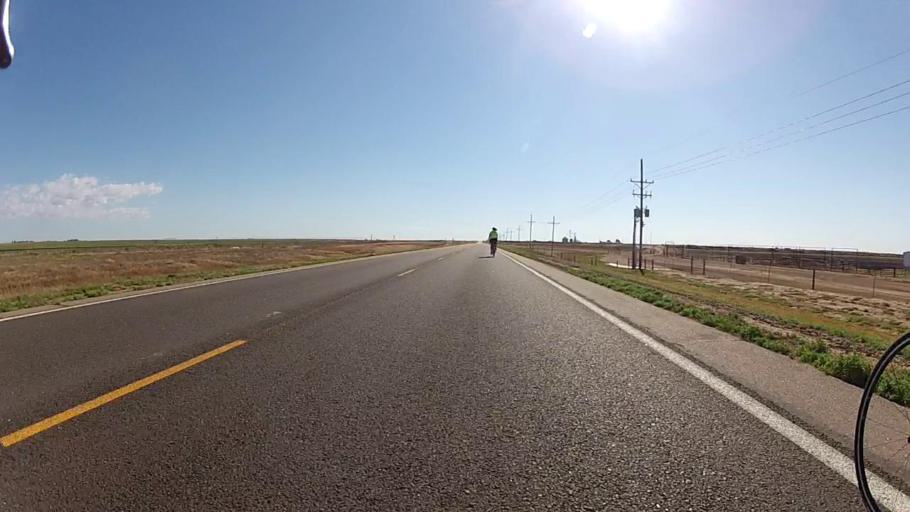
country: US
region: Kansas
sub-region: Gray County
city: Cimarron
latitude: 37.5686
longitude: -100.5455
